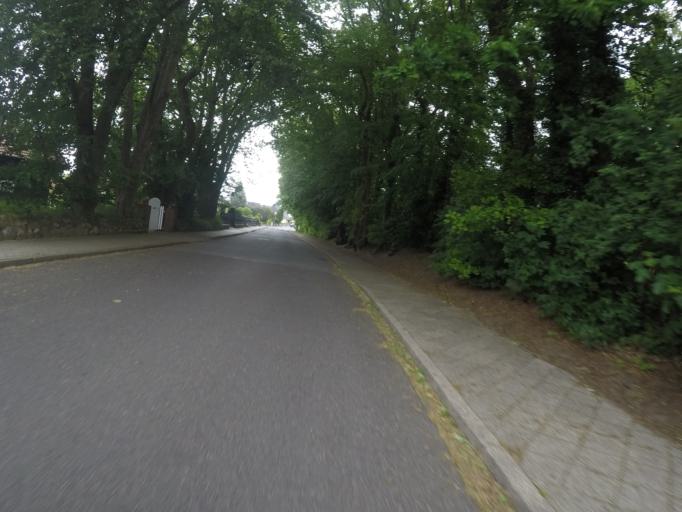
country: DE
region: Schleswig-Holstein
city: Quickborn
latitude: 53.7235
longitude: 9.9123
